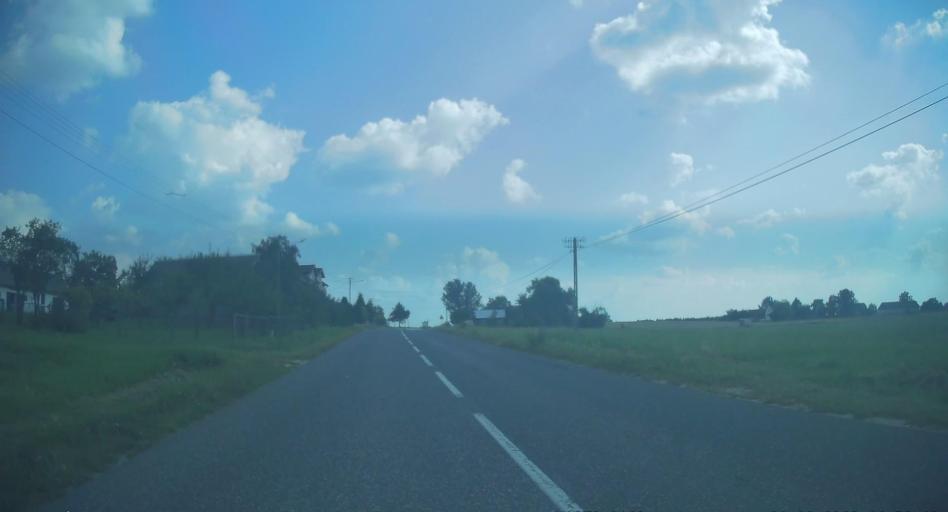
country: PL
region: Swietokrzyskie
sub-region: Powiat kielecki
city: Lopuszno
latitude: 50.9090
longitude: 20.2455
